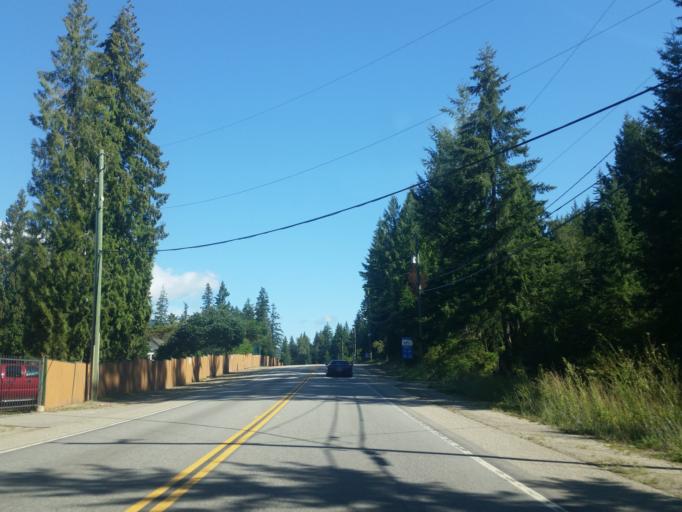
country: CA
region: British Columbia
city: Sicamous
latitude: 50.7195
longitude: -119.0320
